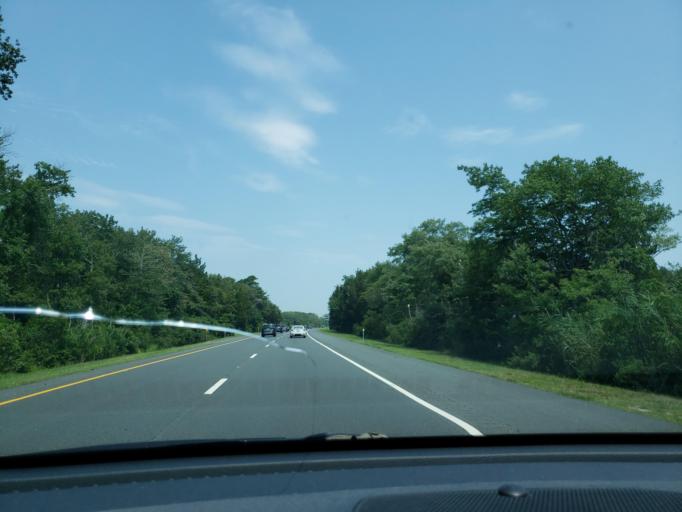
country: US
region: New Jersey
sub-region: Cape May County
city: Sea Isle City
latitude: 39.2113
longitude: -74.6921
